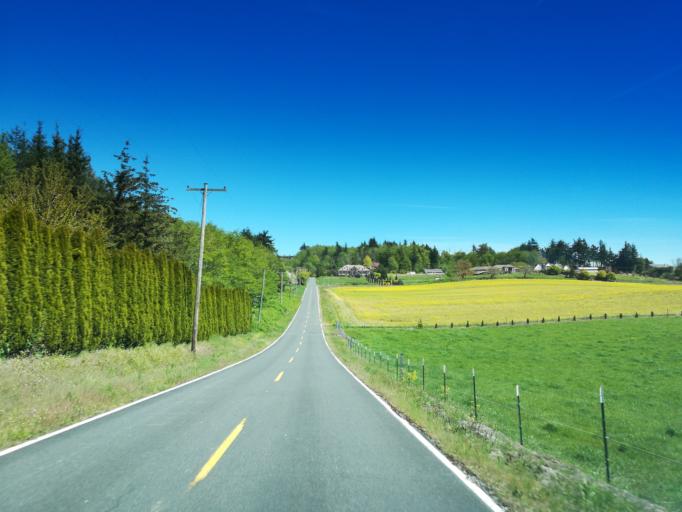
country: US
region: Oregon
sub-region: Multnomah County
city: Troutdale
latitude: 45.5335
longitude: -122.3568
